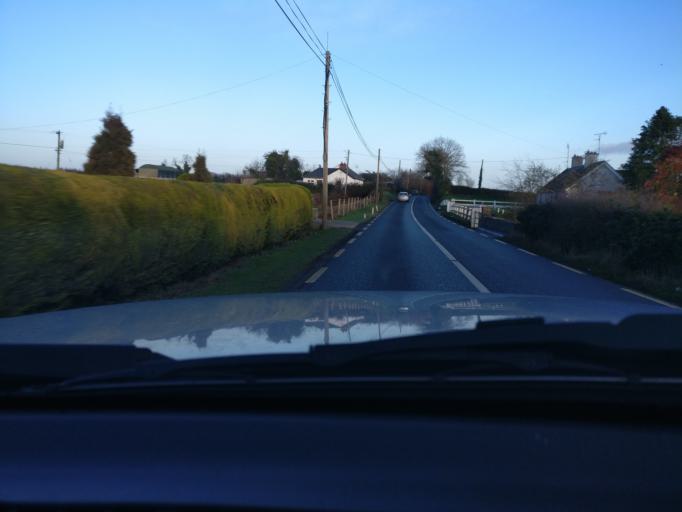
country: IE
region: Leinster
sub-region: Lu
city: Ardee
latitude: 53.8493
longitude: -6.5897
